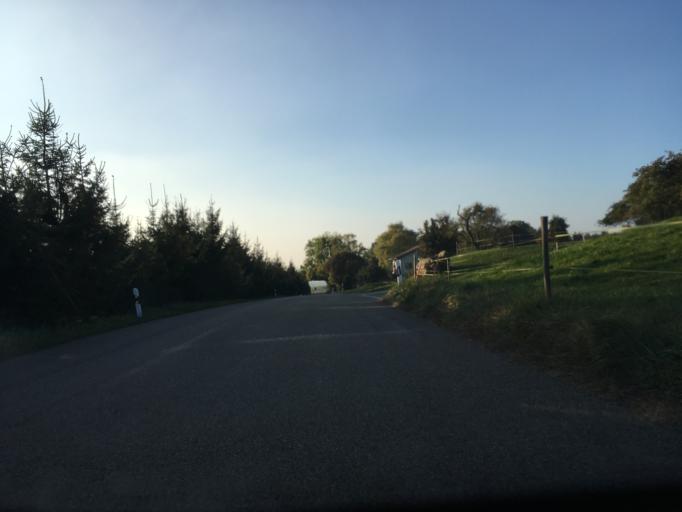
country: CH
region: Zurich
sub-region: Bezirk Pfaeffikon
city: Hittnau / Hittnau (Dorf)
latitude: 47.3597
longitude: 8.8146
